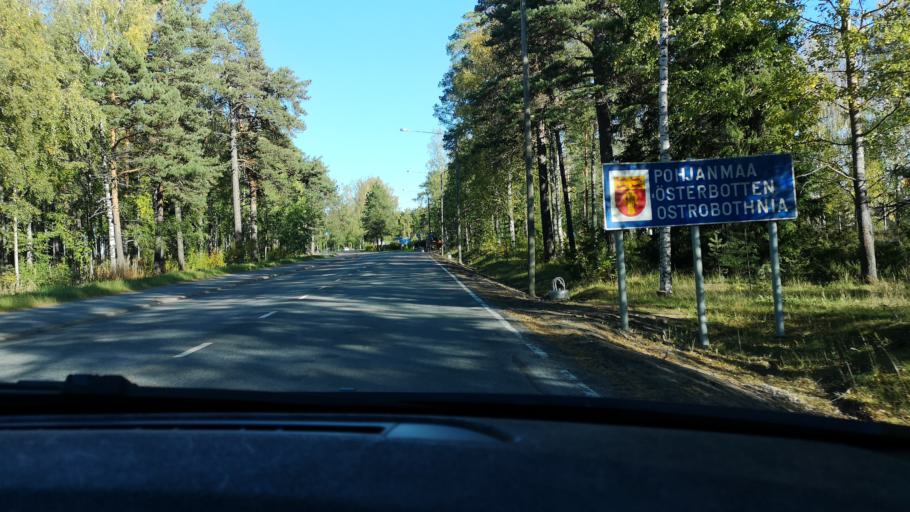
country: FI
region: Ostrobothnia
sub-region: Vaasa
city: Vaasa
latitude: 63.0907
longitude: 21.5836
